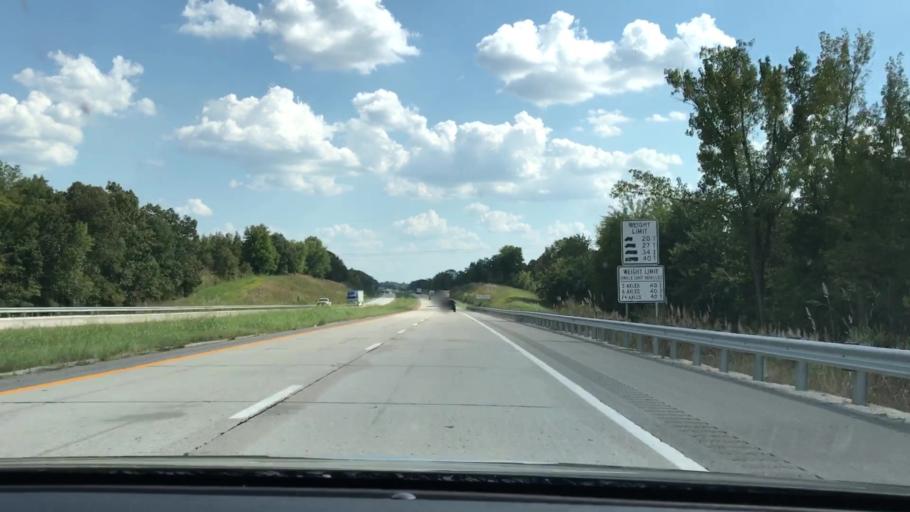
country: US
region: Kentucky
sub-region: Ohio County
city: Oak Grove
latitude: 37.3690
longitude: -86.7999
